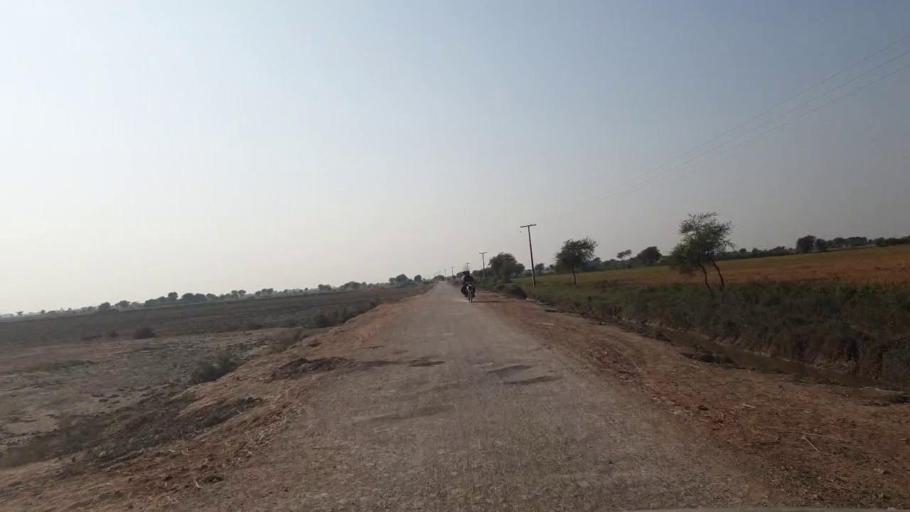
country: PK
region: Sindh
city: Kario
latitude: 24.8919
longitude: 68.6440
